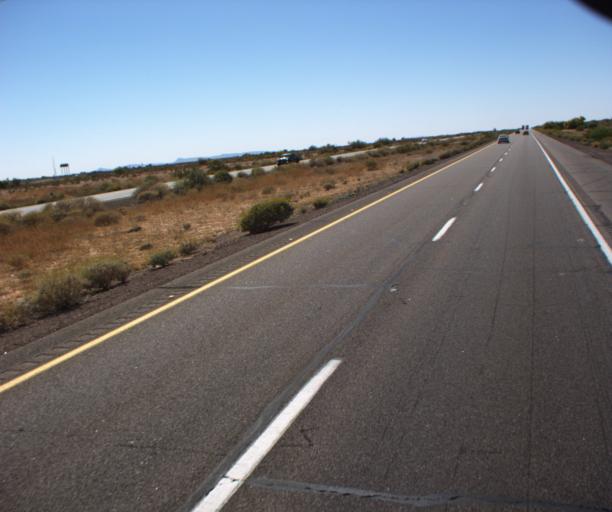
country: US
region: Arizona
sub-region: Maricopa County
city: Gila Bend
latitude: 32.8754
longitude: -113.1234
